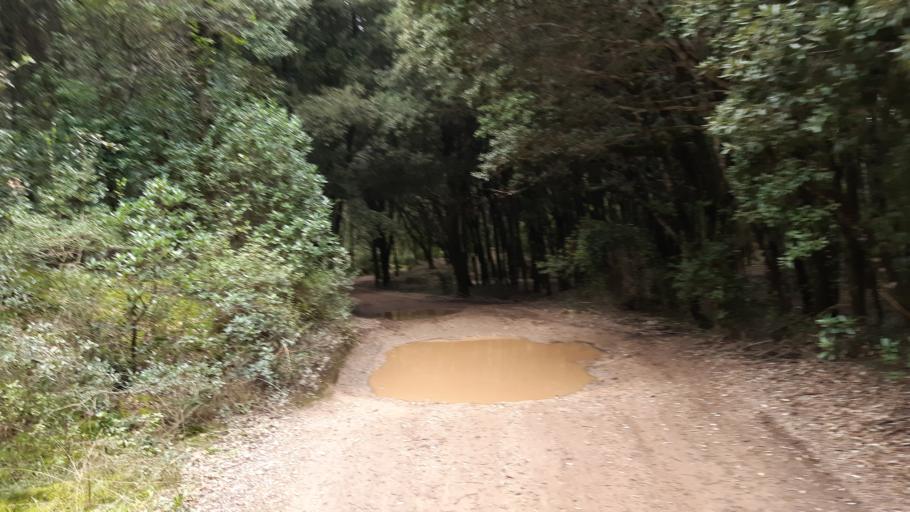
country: IT
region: Sardinia
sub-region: Provincia di Carbonia-Iglesias
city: Iglesias
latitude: 39.3862
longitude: 8.5716
